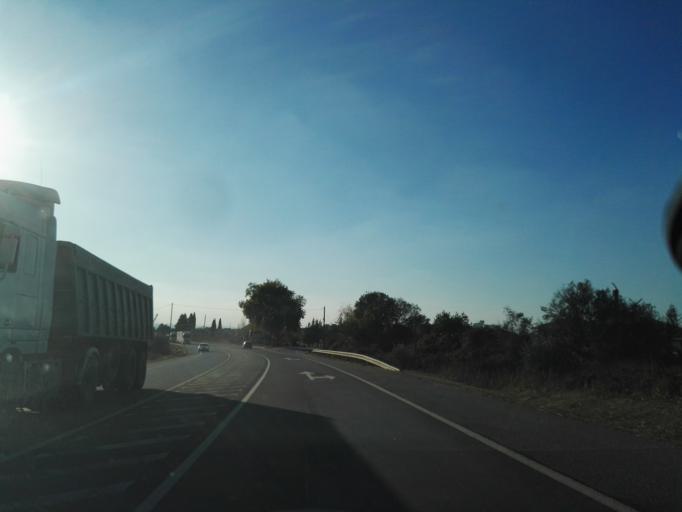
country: PT
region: Evora
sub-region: Estremoz
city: Estremoz
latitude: 38.8362
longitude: -7.5717
